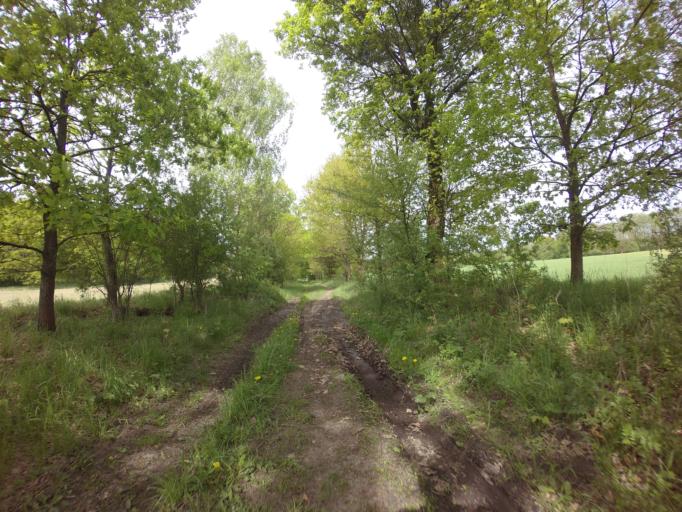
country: PL
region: West Pomeranian Voivodeship
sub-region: Powiat choszczenski
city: Bierzwnik
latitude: 53.1572
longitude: 15.6338
